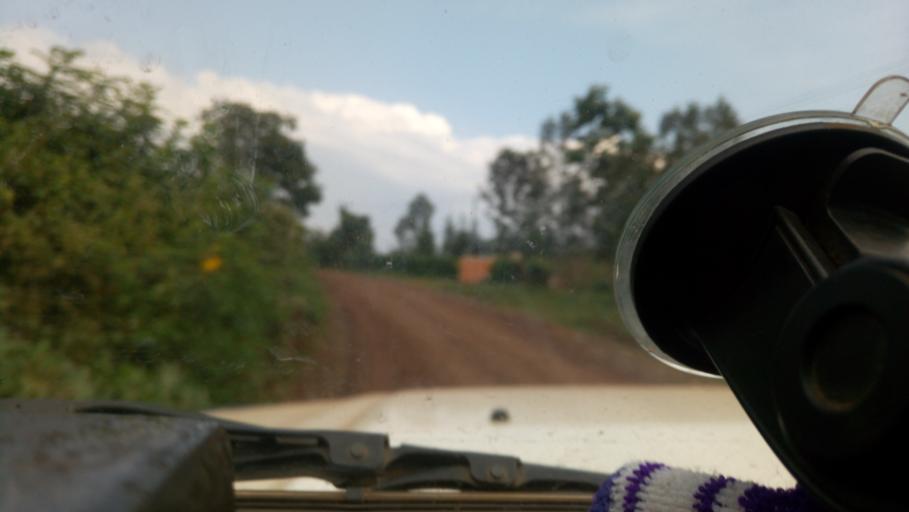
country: KE
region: Kericho
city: Sotik
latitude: -0.6411
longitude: 35.1529
